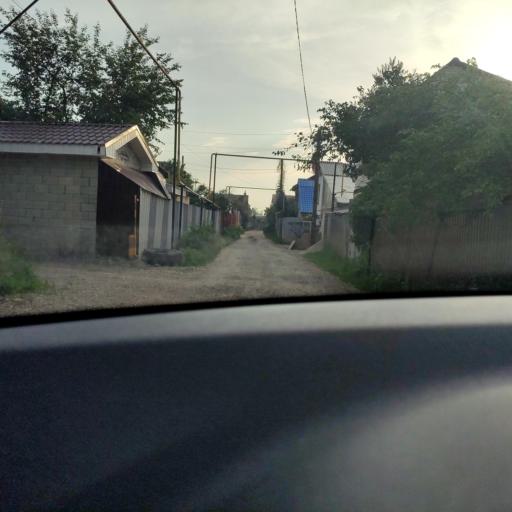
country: RU
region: Samara
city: Novokuybyshevsk
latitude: 53.1516
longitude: 50.0199
